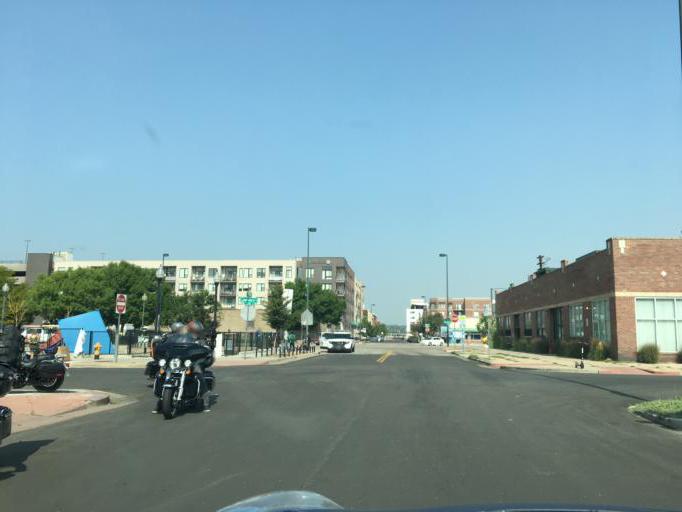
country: US
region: Colorado
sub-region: Denver County
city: Denver
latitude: 39.7558
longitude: -104.9867
